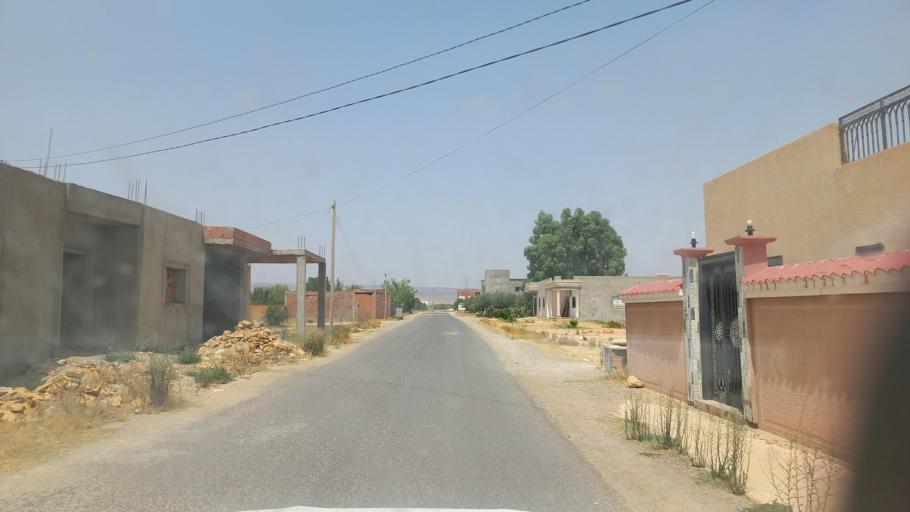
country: TN
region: Al Qasrayn
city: Kasserine
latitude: 35.2520
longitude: 9.0185
